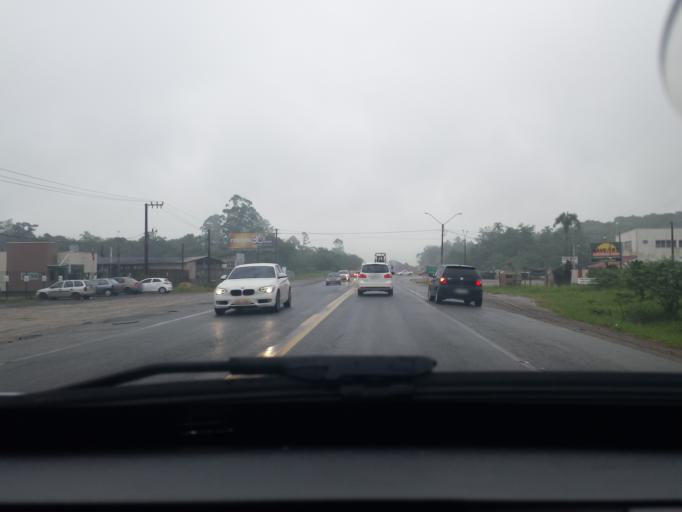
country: BR
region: Santa Catarina
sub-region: Navegantes
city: Navegantes
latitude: -26.8335
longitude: -48.7346
